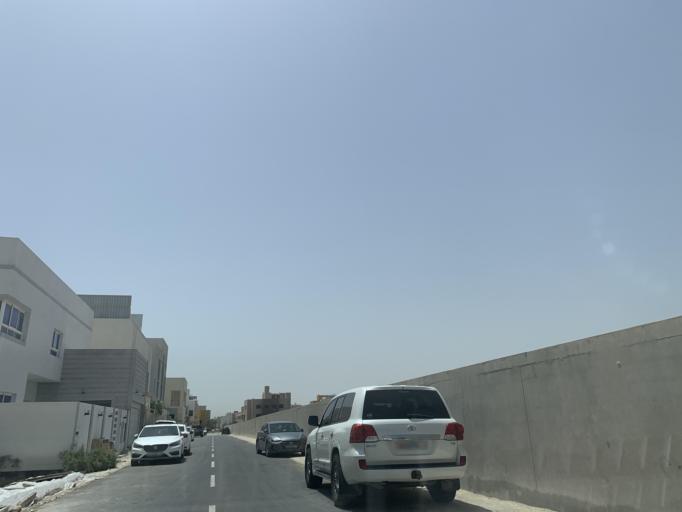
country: BH
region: Northern
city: Madinat `Isa
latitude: 26.1605
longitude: 50.5789
